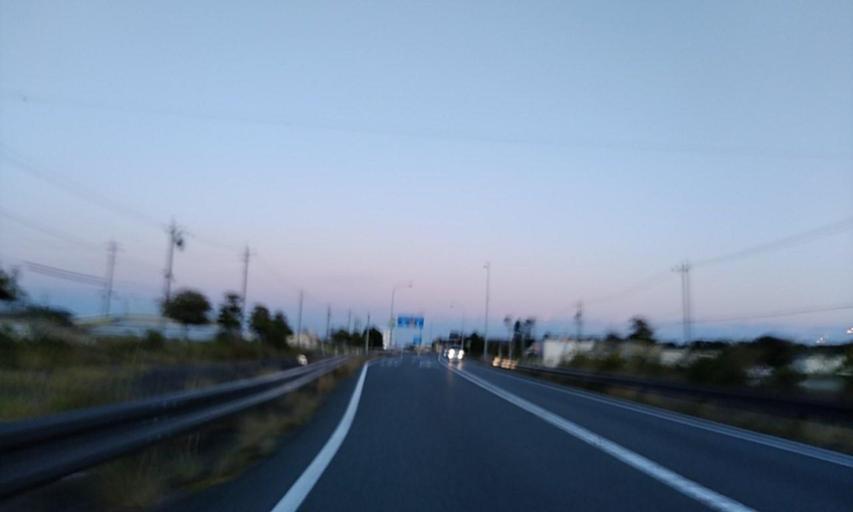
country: JP
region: Shizuoka
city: Hamamatsu
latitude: 34.6808
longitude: 137.6597
